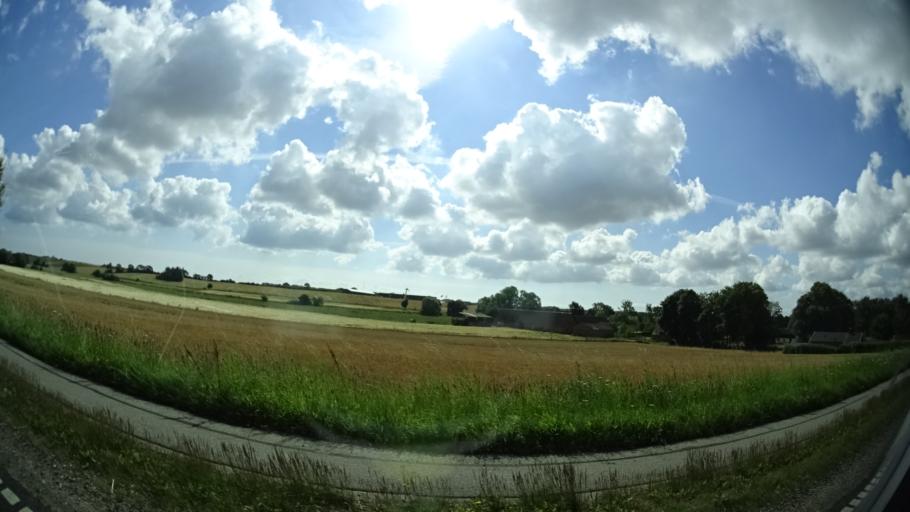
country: DK
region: Central Jutland
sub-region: Odder Kommune
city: Odder
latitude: 55.9932
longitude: 10.1591
